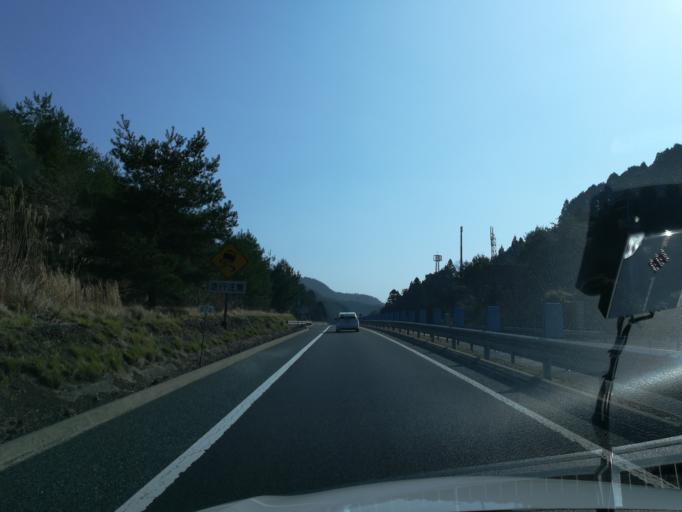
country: JP
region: Tokushima
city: Ikedacho
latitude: 34.0046
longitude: 133.6966
